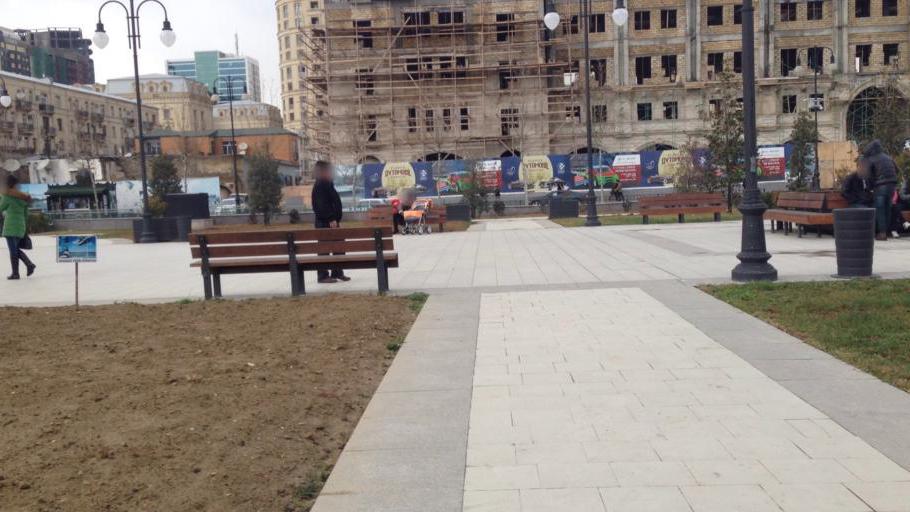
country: AZ
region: Baki
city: Badamdar
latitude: 40.3757
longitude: 49.8344
